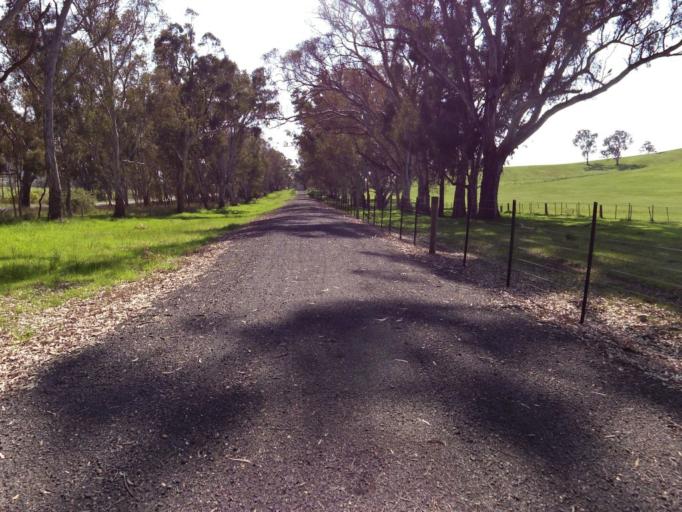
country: AU
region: Victoria
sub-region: Murrindindi
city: Alexandra
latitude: -37.1392
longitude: 145.5905
